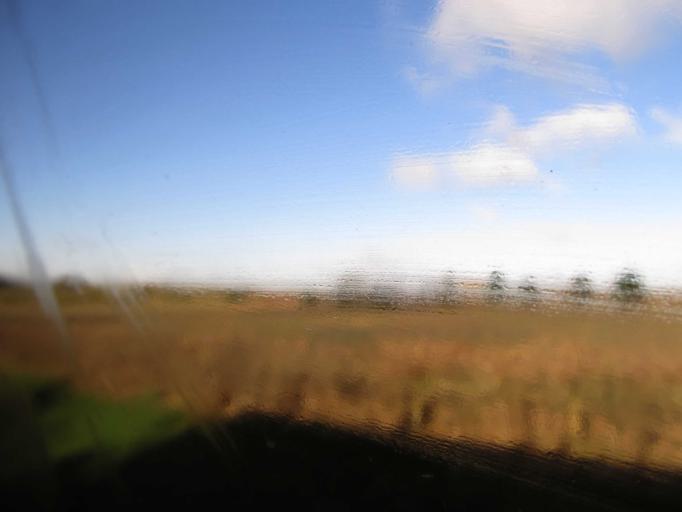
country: GB
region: England
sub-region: Hampshire
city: Kings Worthy
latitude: 51.1656
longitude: -1.3172
